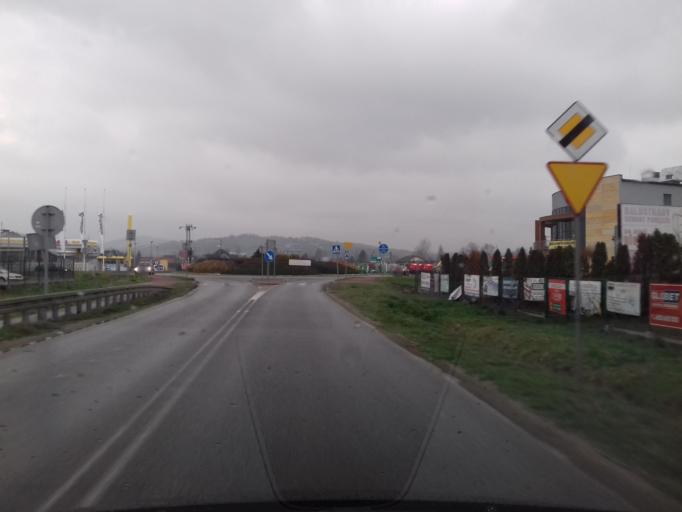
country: PL
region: Lesser Poland Voivodeship
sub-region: Powiat nowosadecki
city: Stary Sacz
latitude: 49.5912
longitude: 20.6298
